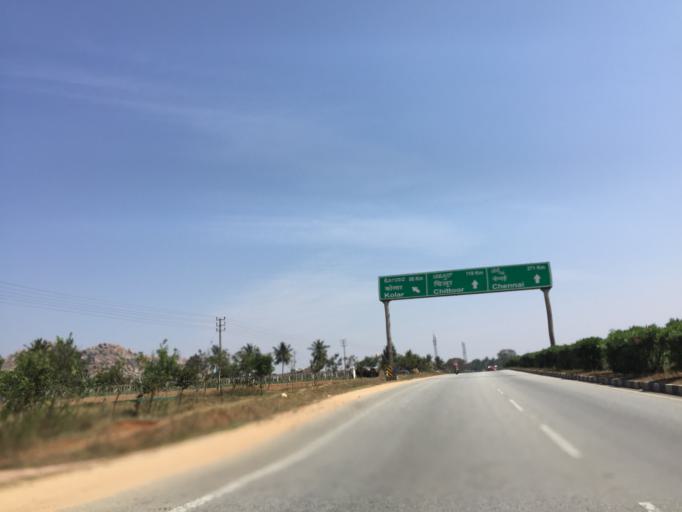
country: IN
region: Karnataka
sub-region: Kolar
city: Kolar
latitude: 13.1211
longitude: 78.0760
